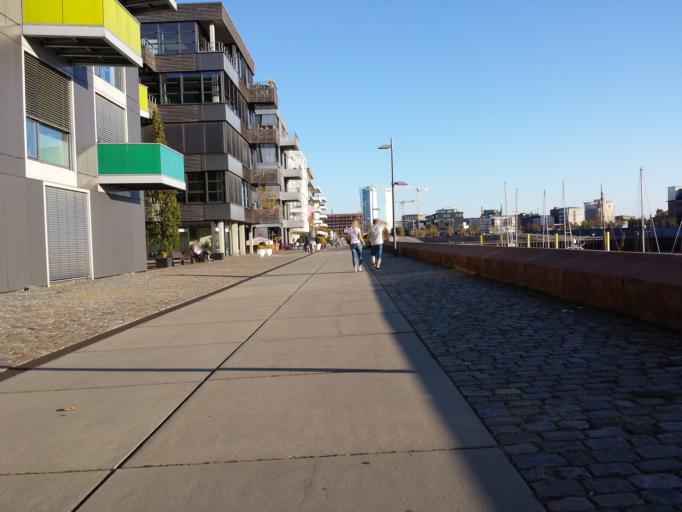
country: DE
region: Bremen
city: Bremen
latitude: 53.0885
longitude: 8.7775
